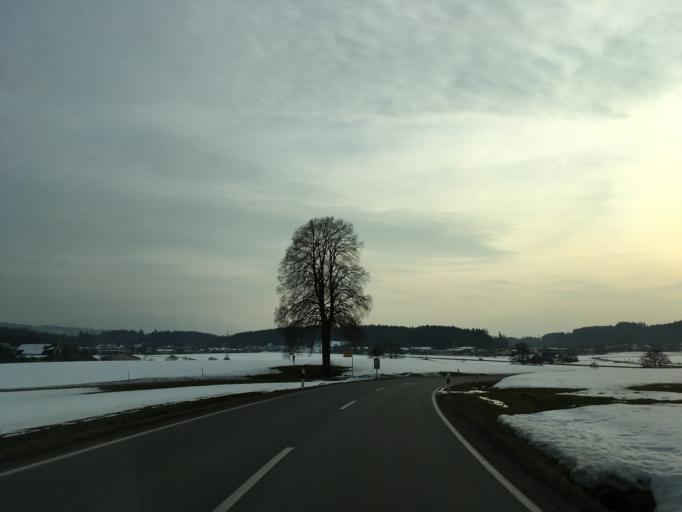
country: DE
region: Bavaria
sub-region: Upper Bavaria
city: Bad Endorf
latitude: 47.9272
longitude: 12.2957
